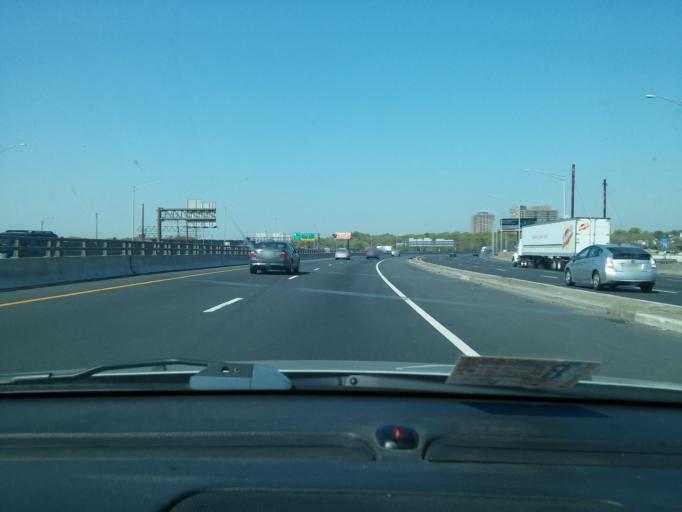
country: US
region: New Jersey
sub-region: Essex County
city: Newark
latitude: 40.7090
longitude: -74.1863
